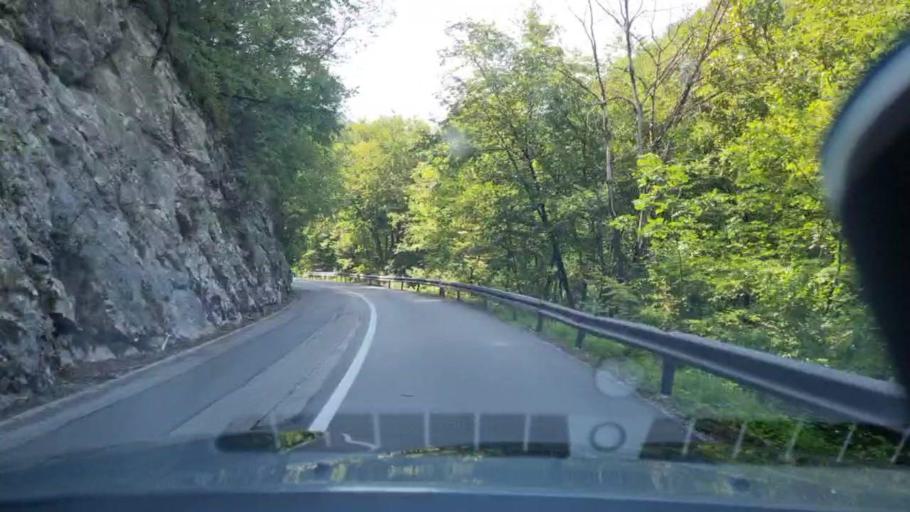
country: BA
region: Federation of Bosnia and Herzegovina
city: Bosanska Krupa
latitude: 44.8721
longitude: 16.0835
